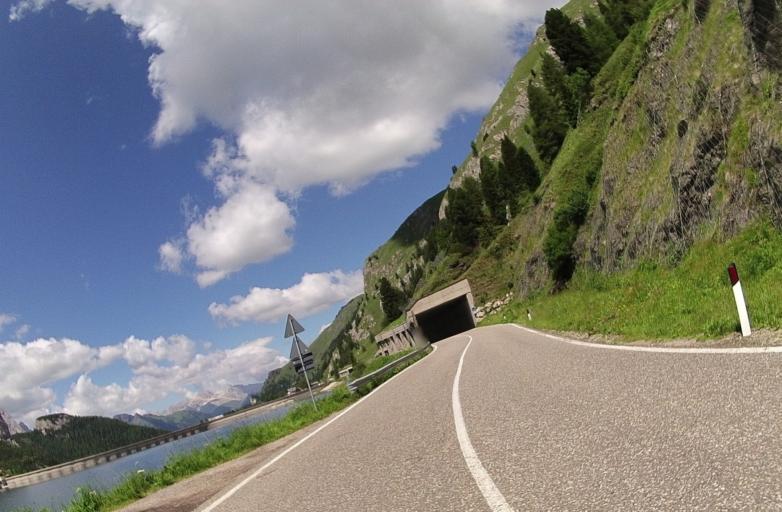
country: IT
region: Veneto
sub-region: Provincia di Belluno
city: Livinallongo del Col di Lana
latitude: 46.4617
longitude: 11.8722
